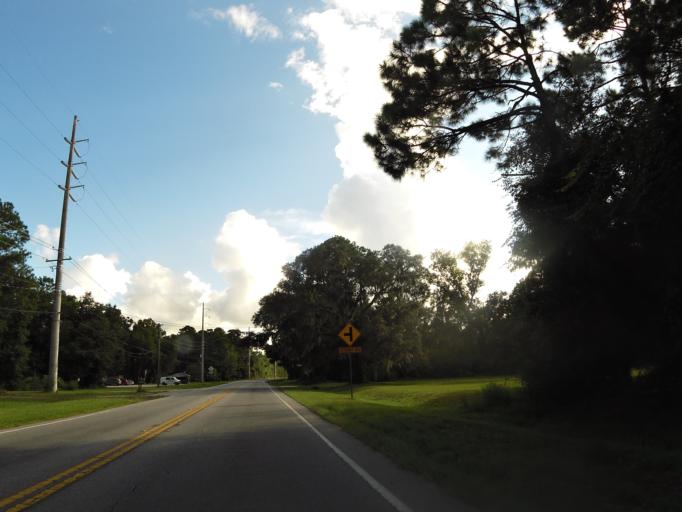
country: US
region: Georgia
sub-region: Glynn County
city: Country Club Estates
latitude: 31.2354
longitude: -81.4522
